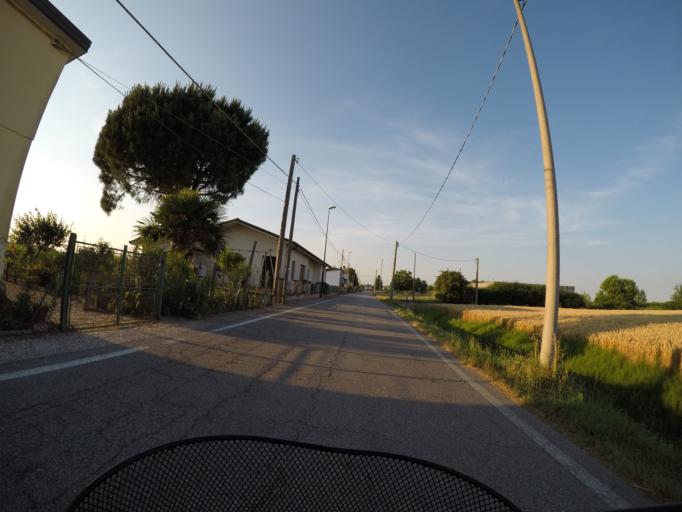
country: IT
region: Veneto
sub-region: Provincia di Rovigo
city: San Bellino
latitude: 45.0219
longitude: 11.5866
